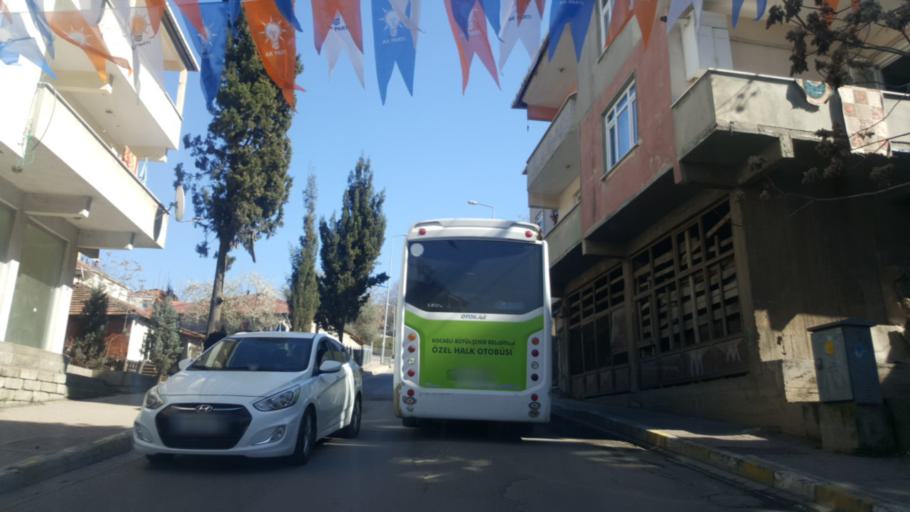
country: TR
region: Kocaeli
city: Tavsancil
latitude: 40.7856
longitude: 29.5497
